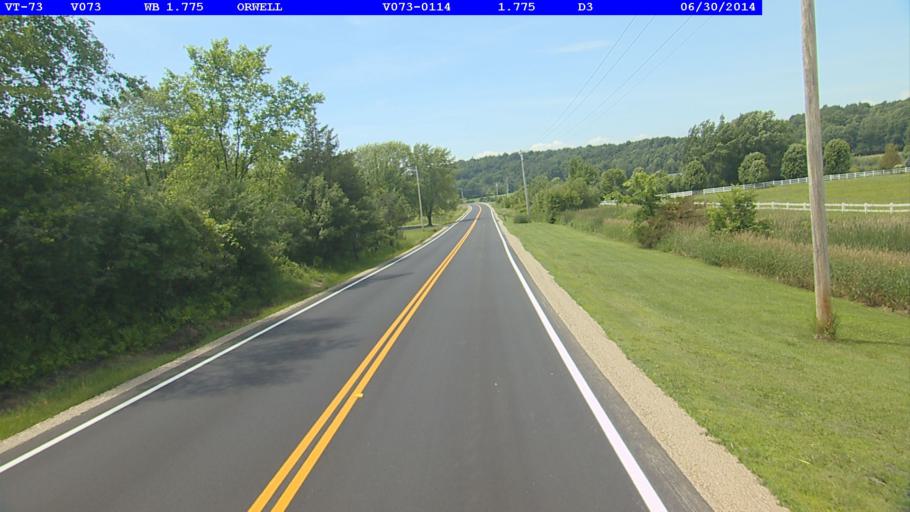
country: US
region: New York
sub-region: Essex County
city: Ticonderoga
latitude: 43.8021
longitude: -73.2706
